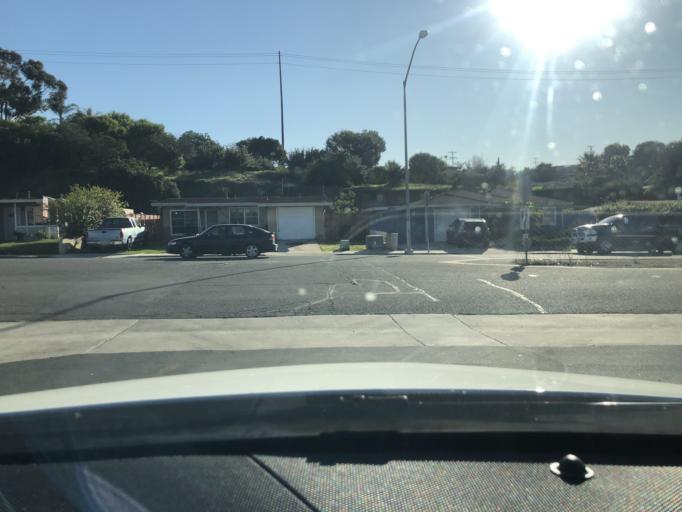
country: US
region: California
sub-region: San Diego County
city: Lemon Grove
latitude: 32.7445
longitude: -117.0638
